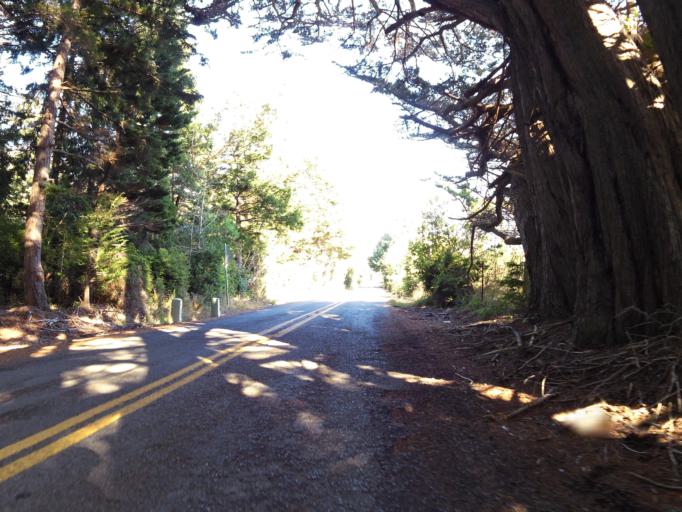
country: US
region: Oregon
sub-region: Coos County
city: Bandon
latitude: 43.0397
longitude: -124.4131
